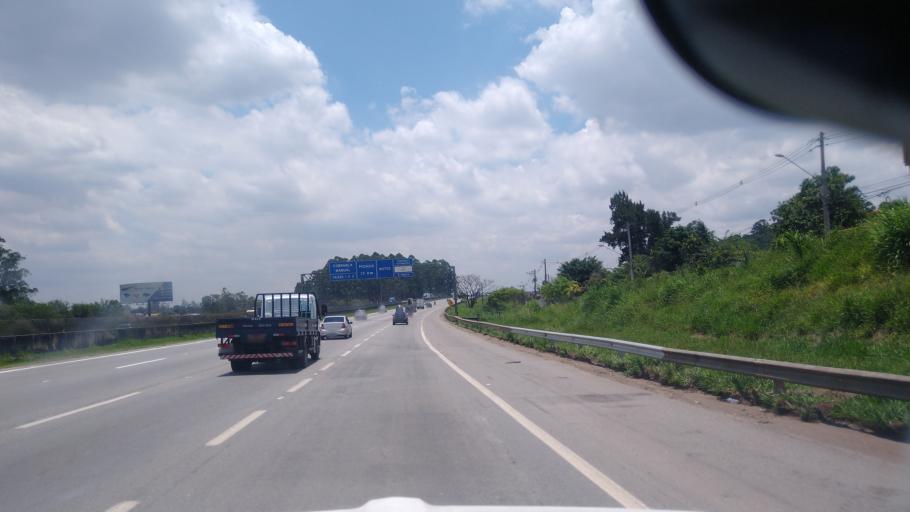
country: BR
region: Sao Paulo
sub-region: Itaquaquecetuba
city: Itaquaquecetuba
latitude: -23.4647
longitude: -46.3490
